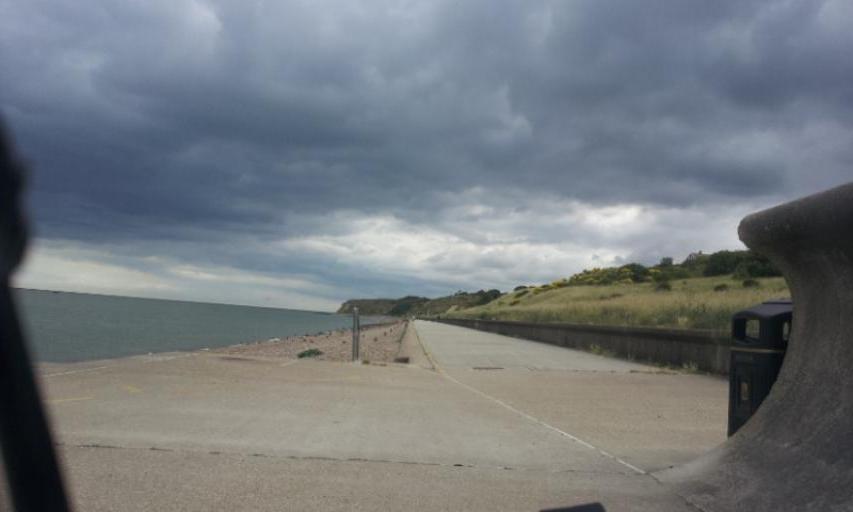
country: GB
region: England
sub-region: Kent
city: Herne Bay
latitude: 51.3739
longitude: 1.1602
